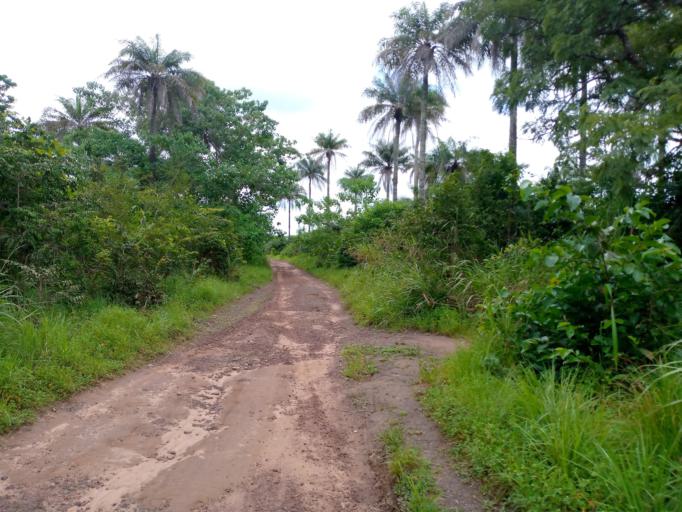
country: SL
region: Northern Province
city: Mange
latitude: 8.9894
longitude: -12.7900
